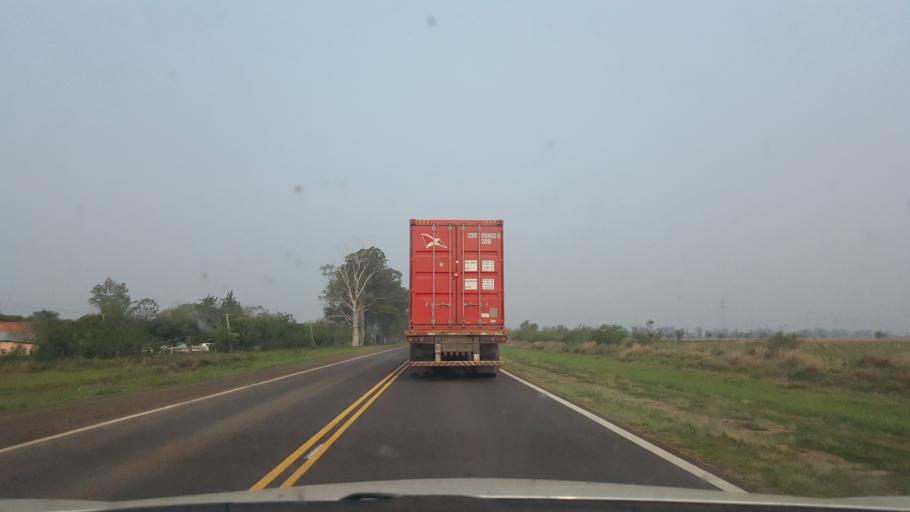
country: AR
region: Corrientes
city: Ita Ibate
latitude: -27.4471
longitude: -57.3340
